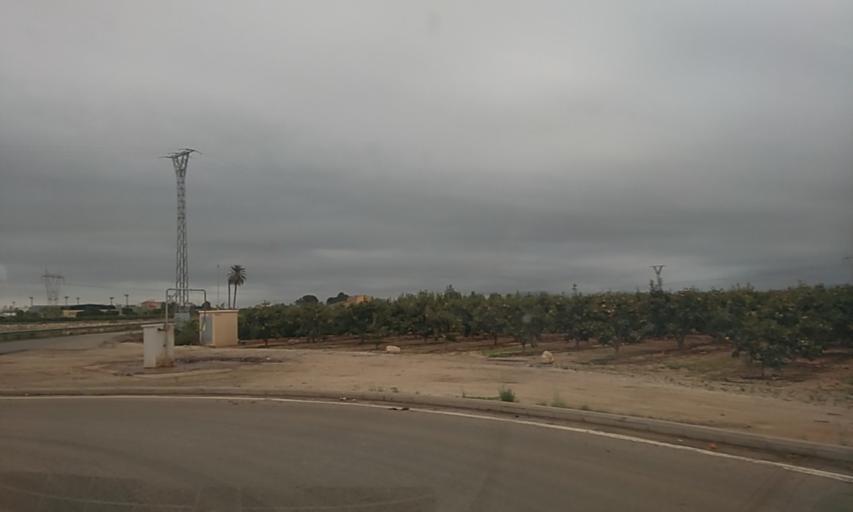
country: ES
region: Valencia
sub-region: Provincia de Valencia
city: L'Alcudia
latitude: 39.1895
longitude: -0.5217
